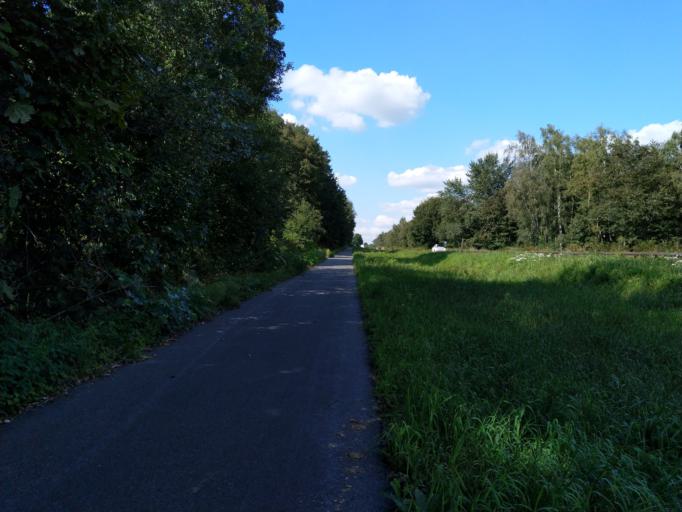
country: BE
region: Wallonia
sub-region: Province du Hainaut
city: Saint-Ghislain
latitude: 50.4848
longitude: 3.8104
